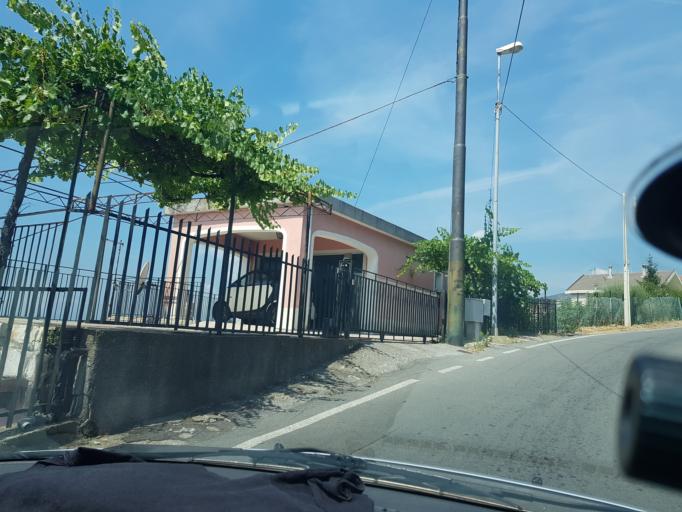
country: IT
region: Liguria
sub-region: Provincia di Genova
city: San Teodoro
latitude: 44.4389
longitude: 8.8383
